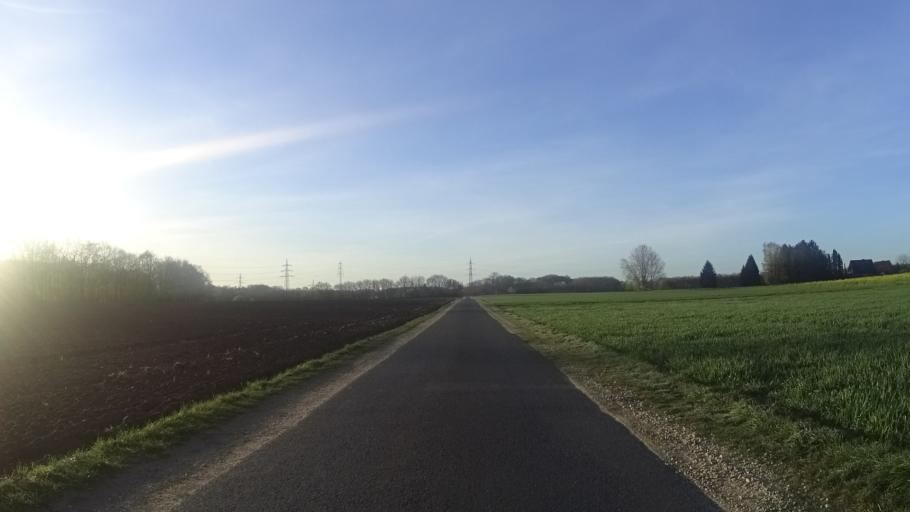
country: DE
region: North Rhine-Westphalia
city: Emsdetten
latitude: 52.2259
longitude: 7.5026
